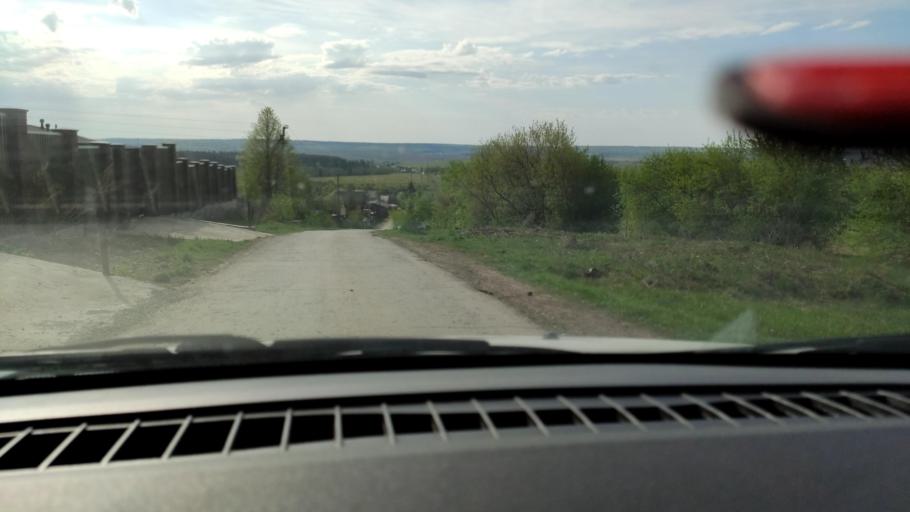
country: RU
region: Perm
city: Froly
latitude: 57.9482
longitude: 56.2962
